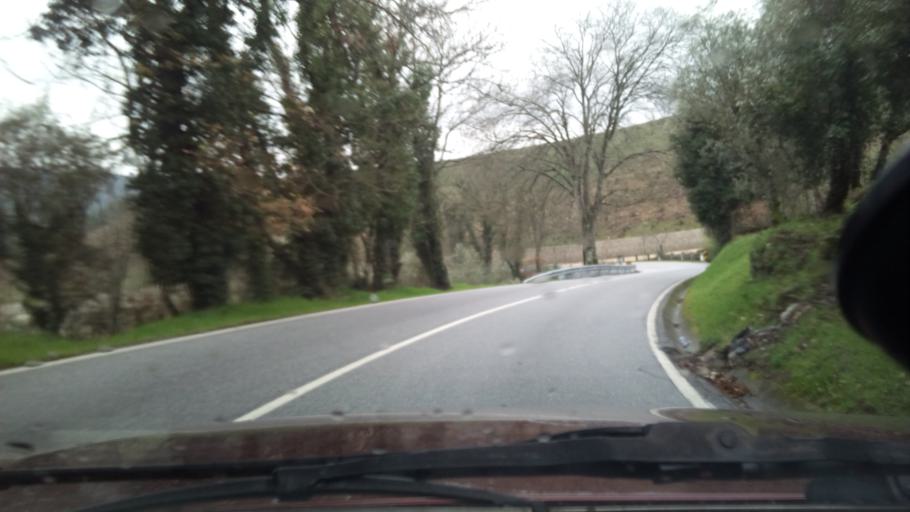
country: PT
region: Viseu
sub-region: Viseu
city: Rio de Loba
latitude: 40.6368
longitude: -7.8321
